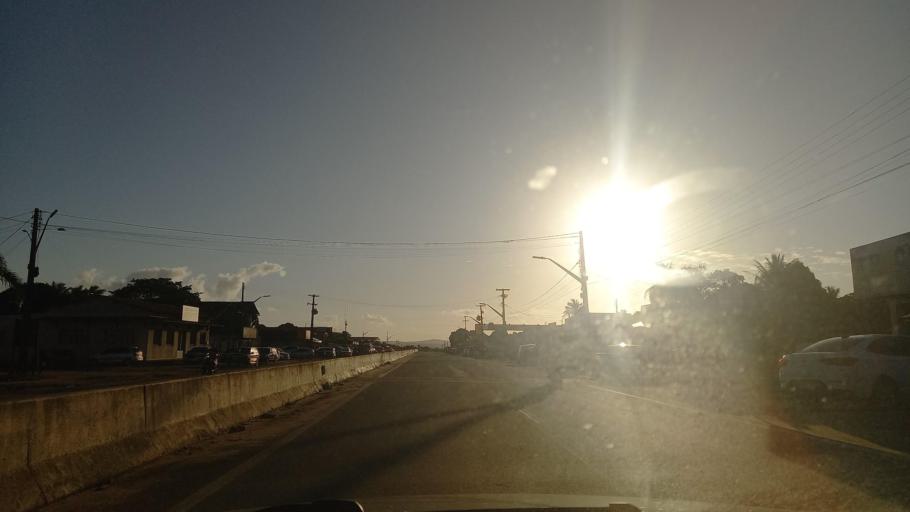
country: BR
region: Alagoas
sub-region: Limoeiro De Anadia
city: Cajueiro
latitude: -9.7426
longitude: -36.4692
